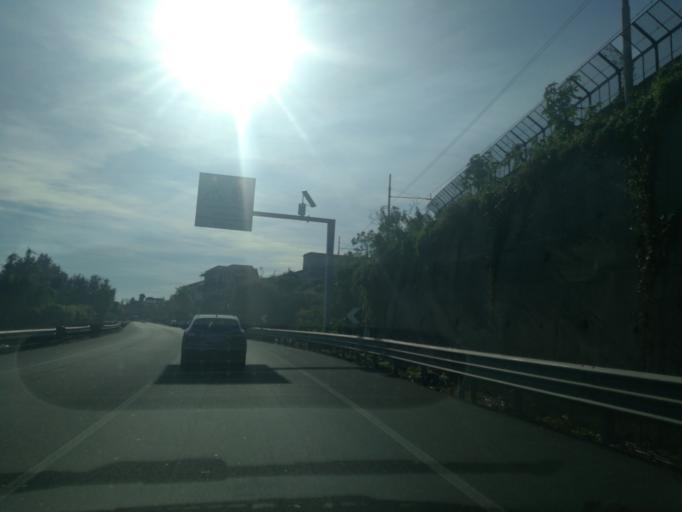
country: IT
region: Sicily
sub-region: Catania
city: Acireale
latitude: 37.6107
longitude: 15.1698
